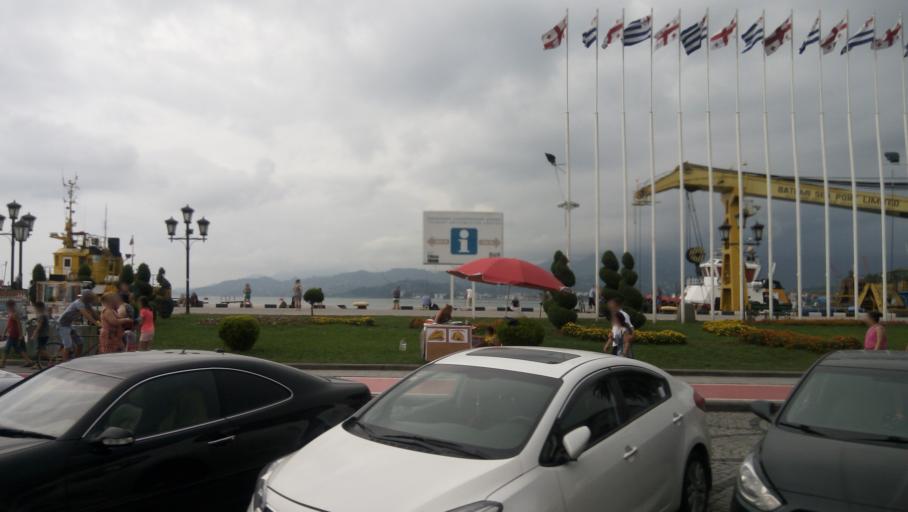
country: GE
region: Ajaria
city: Batumi
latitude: 41.6501
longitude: 41.6445
